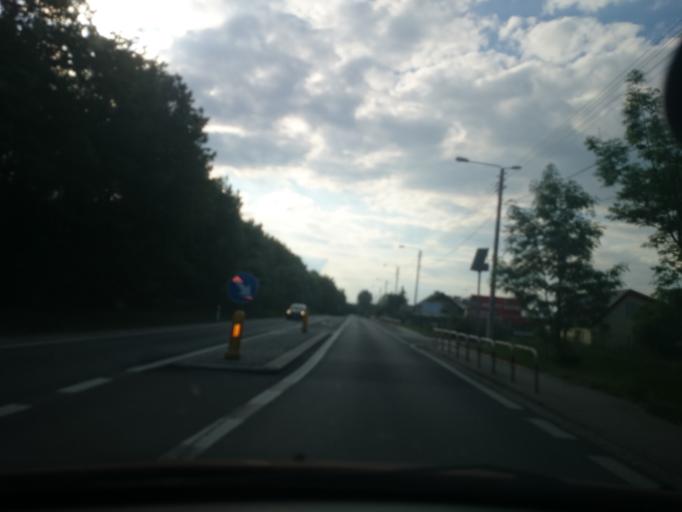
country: PL
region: Opole Voivodeship
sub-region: Powiat opolski
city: Tarnow Opolski
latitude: 50.5997
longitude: 18.0858
